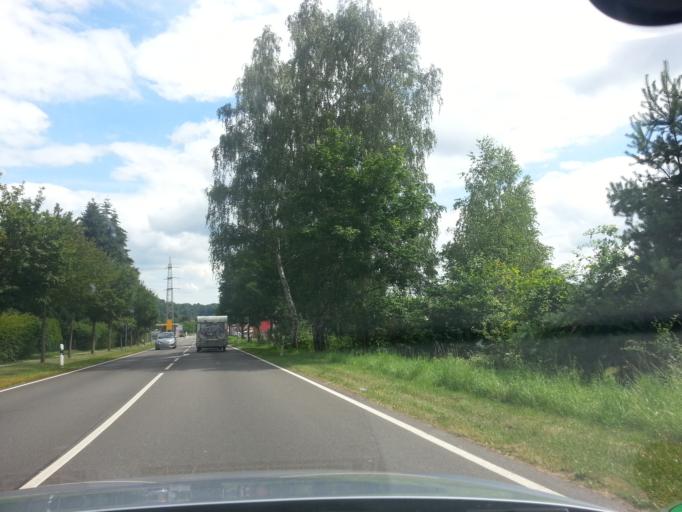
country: DE
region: Saarland
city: Merzig
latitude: 49.4625
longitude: 6.6220
